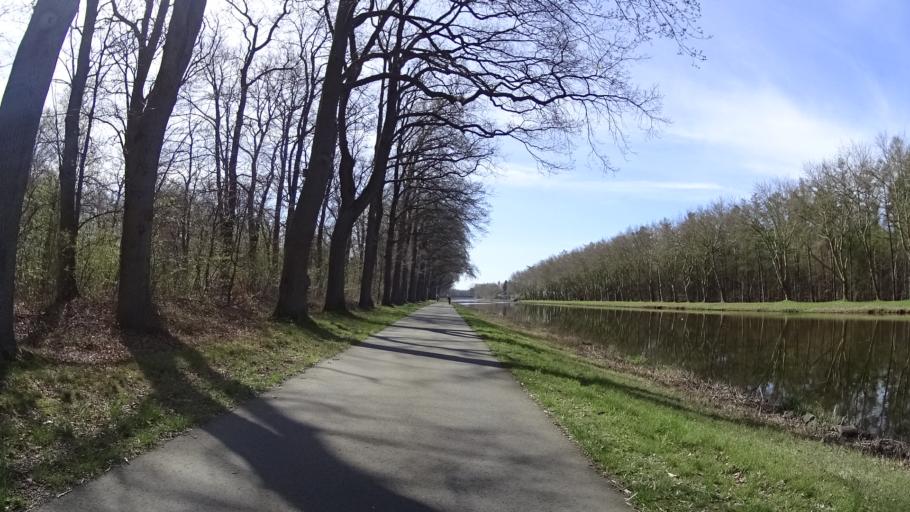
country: DE
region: Lower Saxony
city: Geeste
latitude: 52.5857
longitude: 7.3110
